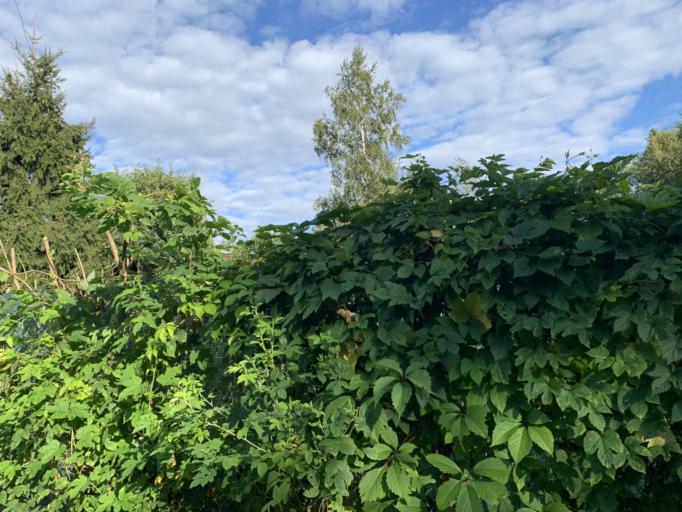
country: RU
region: Moskovskaya
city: Podosinki
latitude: 56.1770
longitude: 37.5750
